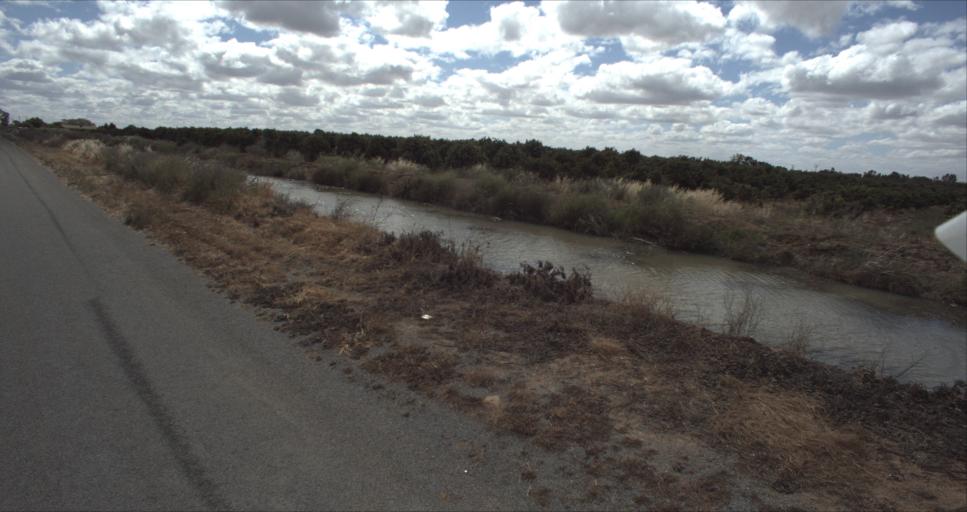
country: AU
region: New South Wales
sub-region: Leeton
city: Leeton
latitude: -34.5806
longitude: 146.3961
